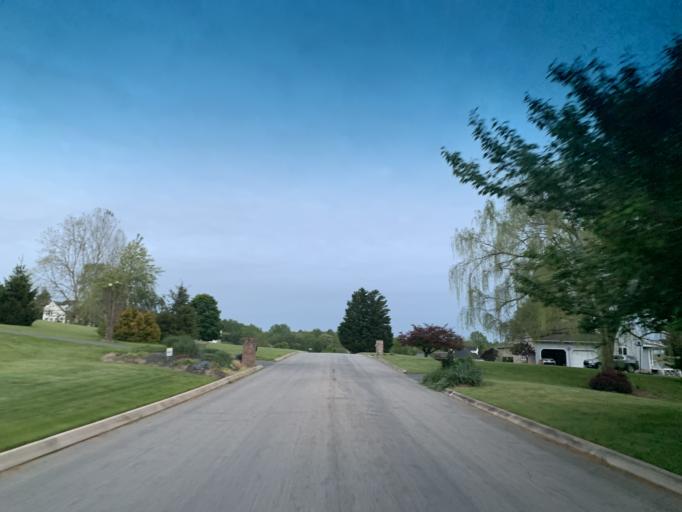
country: US
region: Maryland
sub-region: Harford County
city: South Bel Air
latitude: 39.5920
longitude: -76.2687
